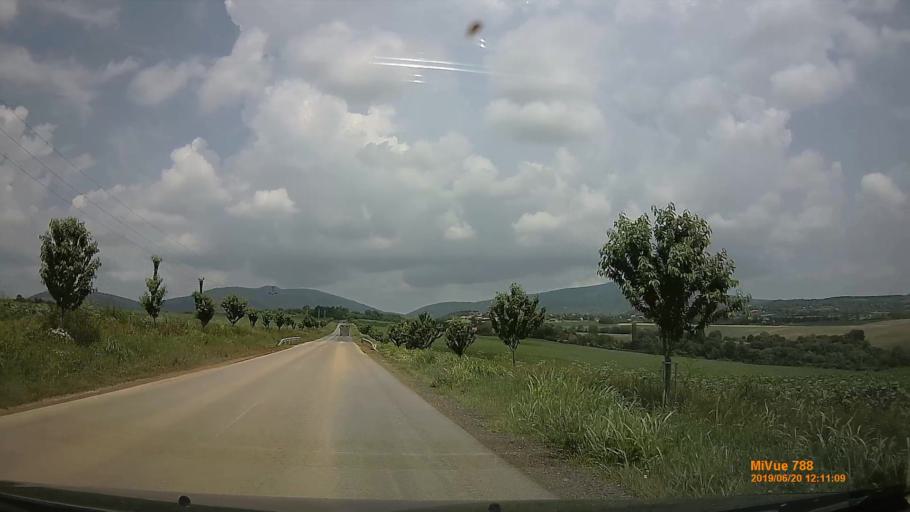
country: HU
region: Baranya
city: Hosszuheteny
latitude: 46.1330
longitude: 18.3482
